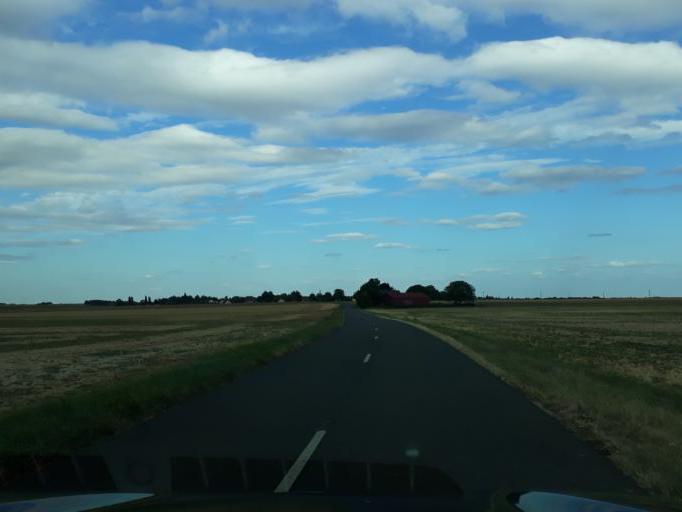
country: FR
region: Centre
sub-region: Departement du Loir-et-Cher
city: Mer
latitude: 47.7982
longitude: 1.4745
